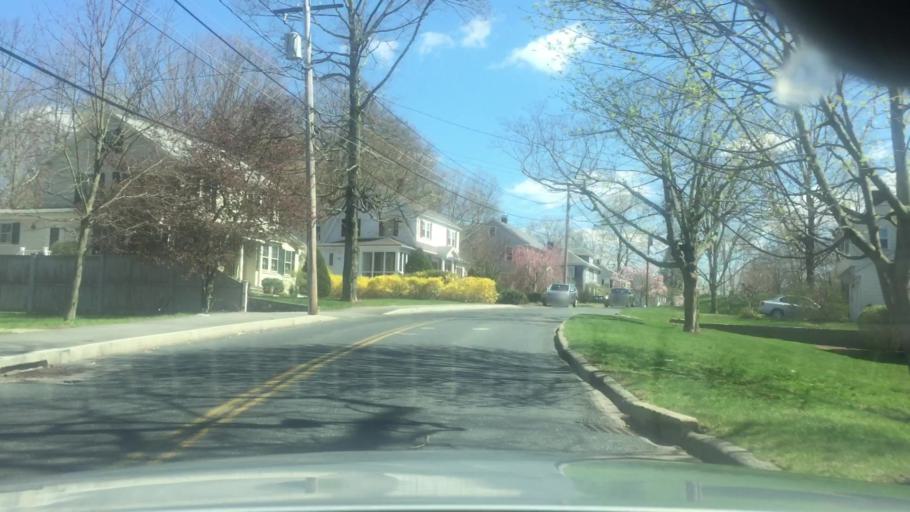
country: US
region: Massachusetts
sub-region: Norfolk County
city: Needham
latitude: 42.2829
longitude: -71.2411
